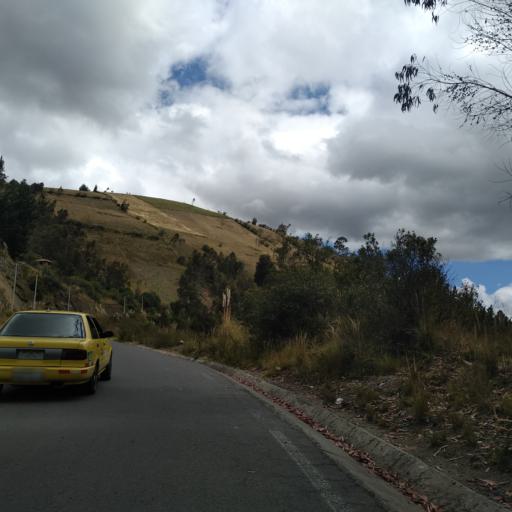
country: EC
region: Cotopaxi
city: Saquisili
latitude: -0.7513
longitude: -78.7247
